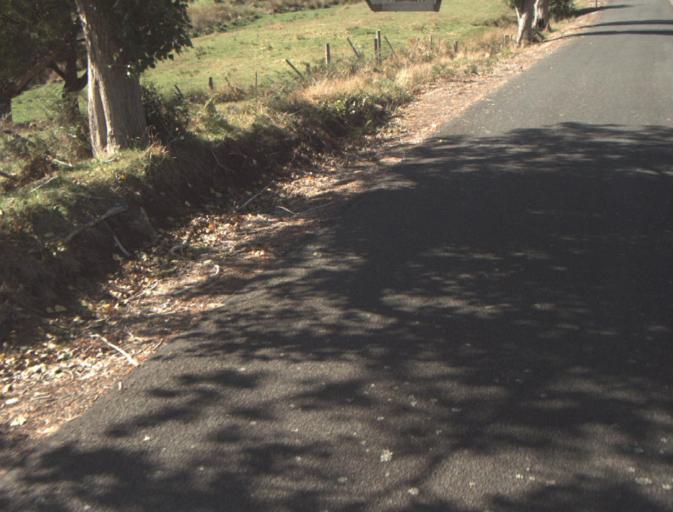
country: AU
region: Tasmania
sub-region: Launceston
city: Mayfield
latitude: -41.2884
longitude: 147.2101
